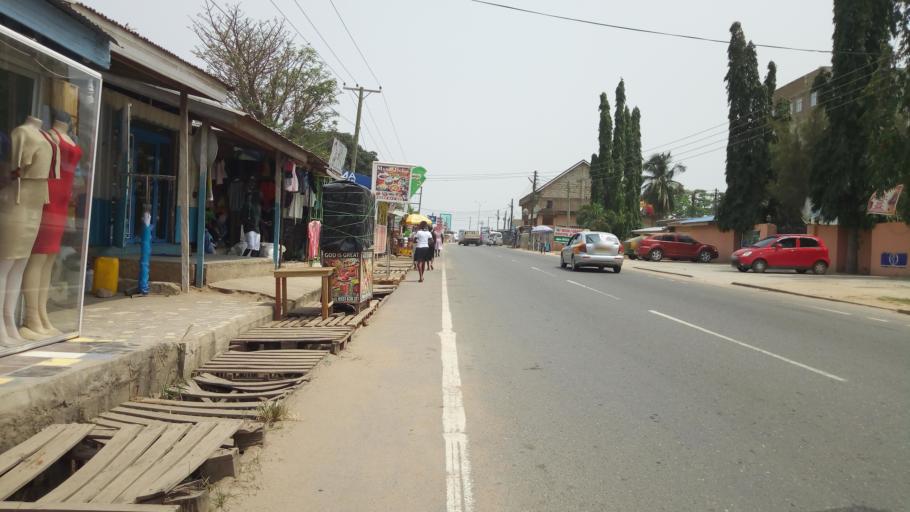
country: GH
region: Greater Accra
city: Gbawe
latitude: 5.5569
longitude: -0.3047
